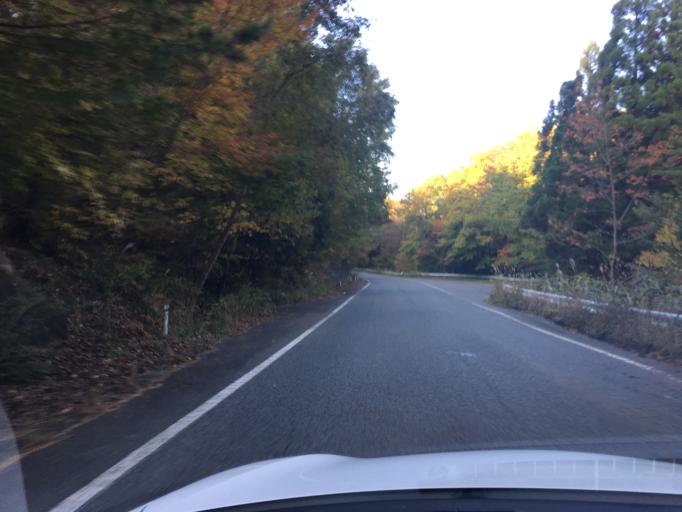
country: JP
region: Fukushima
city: Funehikimachi-funehiki
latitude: 37.2849
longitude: 140.7609
